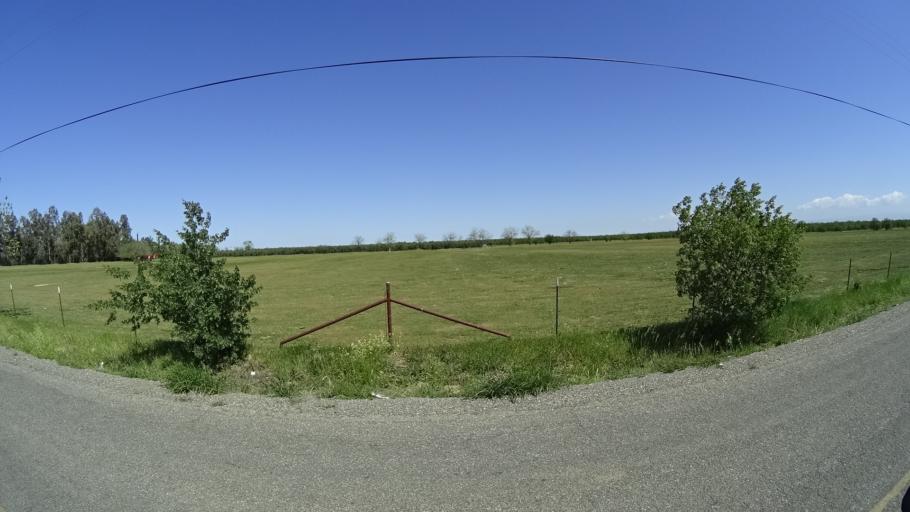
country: US
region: California
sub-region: Glenn County
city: Orland
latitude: 39.6962
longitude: -122.1704
